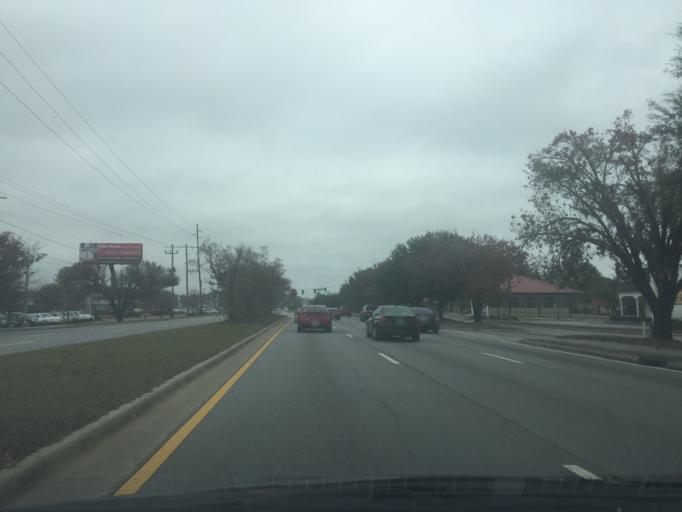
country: US
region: Georgia
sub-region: Chatham County
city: Montgomery
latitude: 31.9902
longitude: -81.1304
